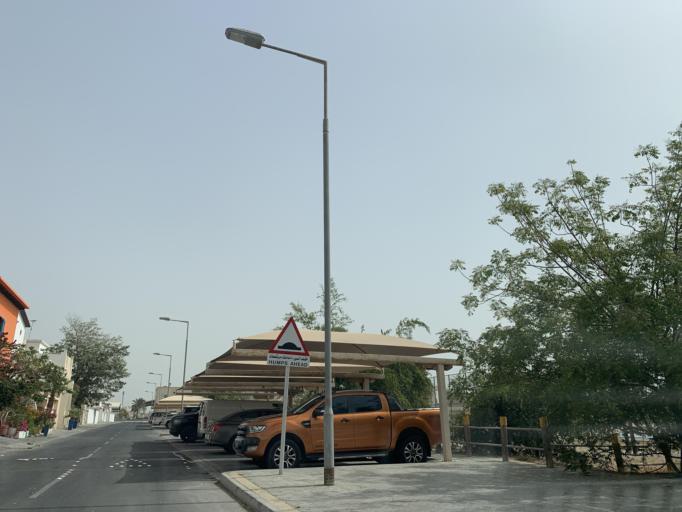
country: BH
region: Northern
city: Madinat `Isa
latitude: 26.1666
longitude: 50.5547
